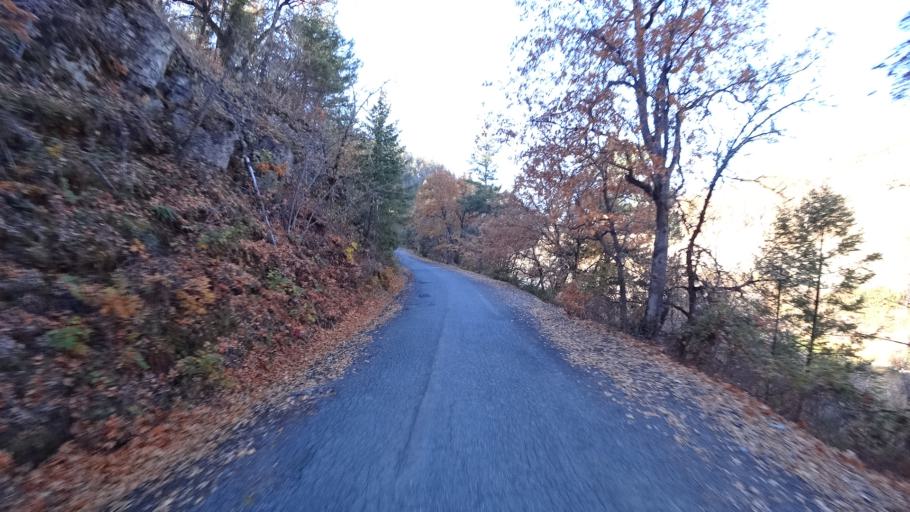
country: US
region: California
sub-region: Siskiyou County
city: Yreka
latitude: 41.8414
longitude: -122.9146
